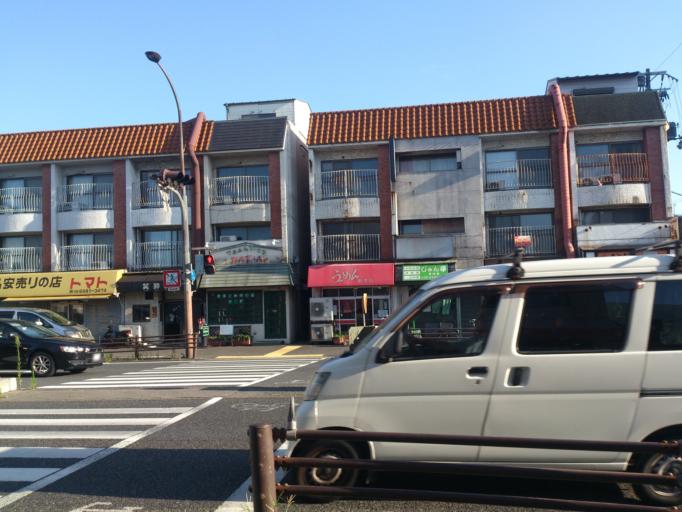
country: JP
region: Hyogo
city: Amagasaki
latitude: 34.7196
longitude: 135.4243
